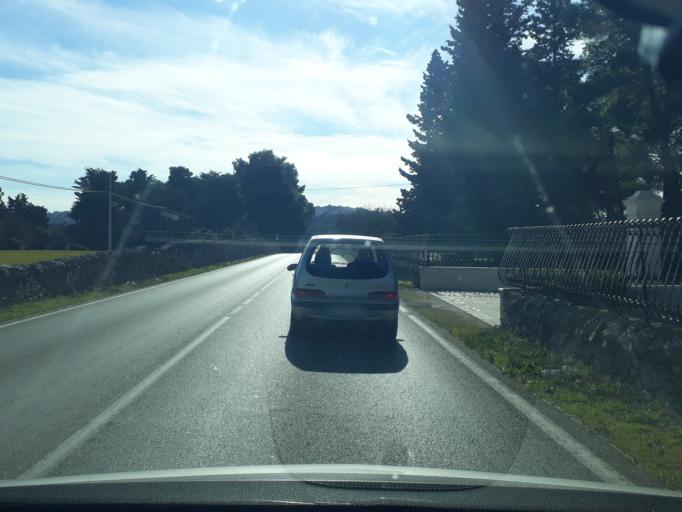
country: IT
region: Apulia
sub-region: Provincia di Taranto
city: Martina Franca
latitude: 40.7233
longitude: 17.3327
